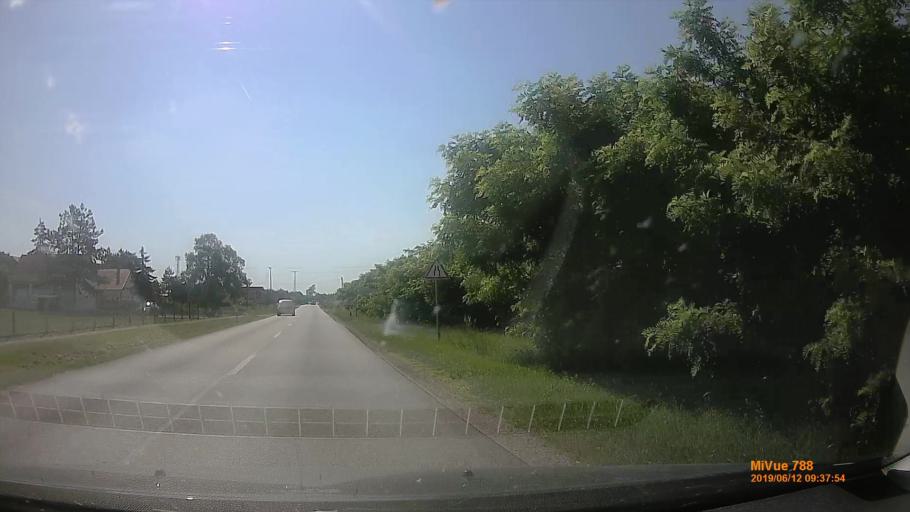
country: HU
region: Pest
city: Gyal
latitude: 47.3723
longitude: 19.2280
